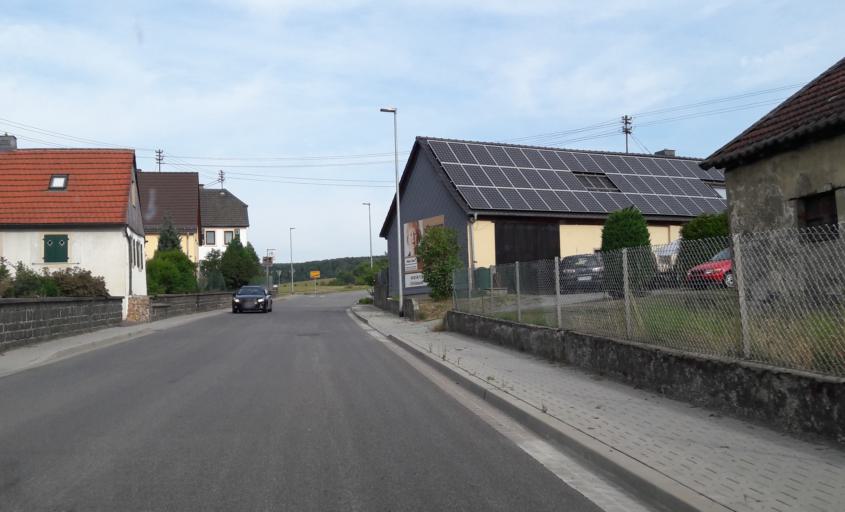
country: DE
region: Rheinland-Pfalz
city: Ellenberg
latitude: 49.6541
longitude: 7.1520
